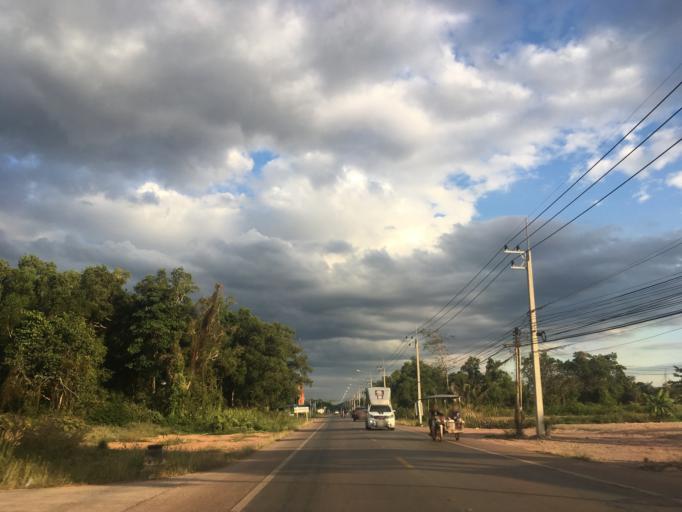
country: TH
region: Chanthaburi
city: Na Yai Am
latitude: 12.6894
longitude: 101.8148
